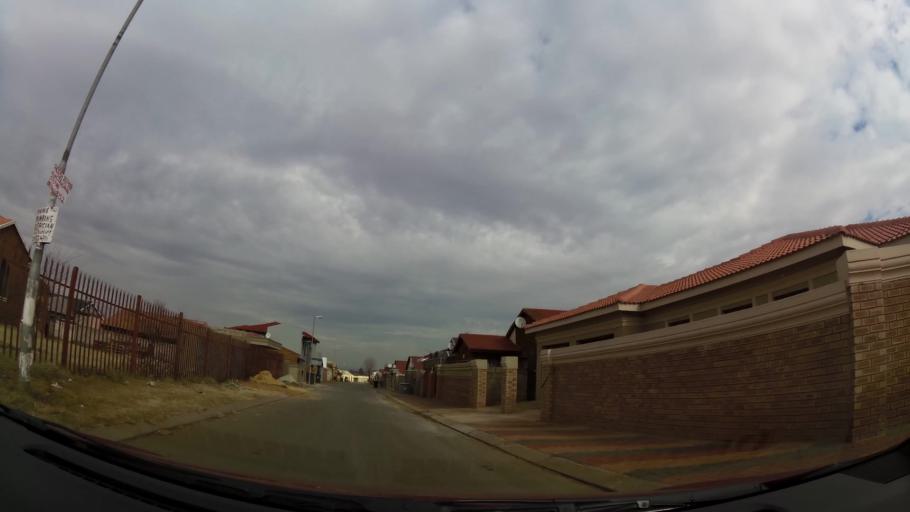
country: ZA
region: Gauteng
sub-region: City of Johannesburg Metropolitan Municipality
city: Soweto
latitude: -26.2742
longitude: 27.8314
